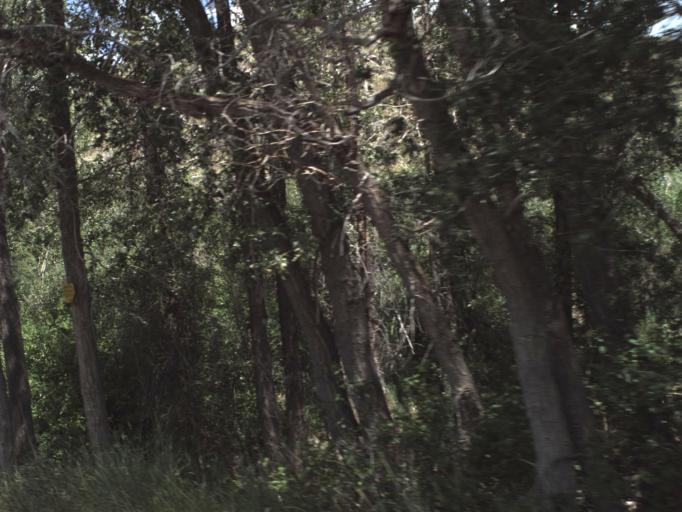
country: US
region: Utah
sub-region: Weber County
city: Wolf Creek
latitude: 41.3489
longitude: -111.5966
